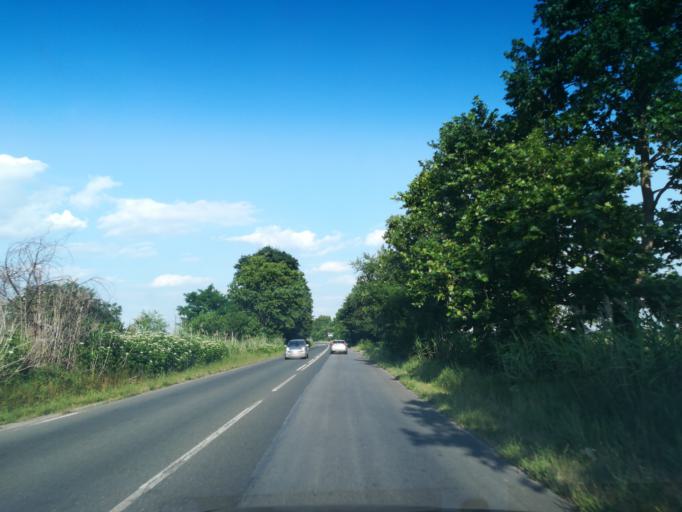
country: BG
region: Plovdiv
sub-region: Obshtina Sadovo
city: Sadovo
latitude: 42.1468
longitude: 24.8435
